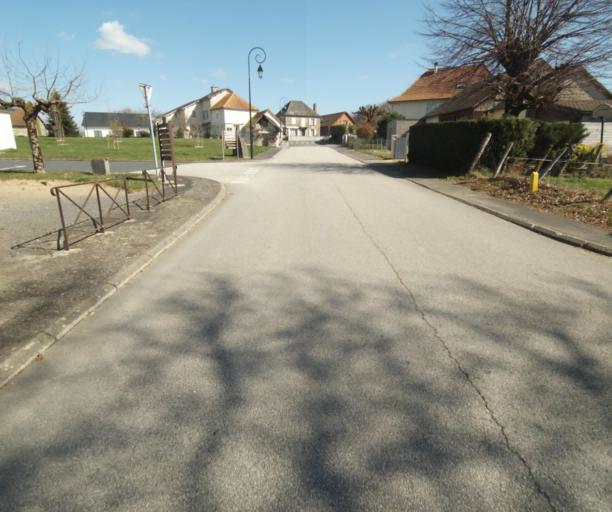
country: FR
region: Limousin
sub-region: Departement de la Correze
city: Saint-Mexant
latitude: 45.2846
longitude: 1.6570
